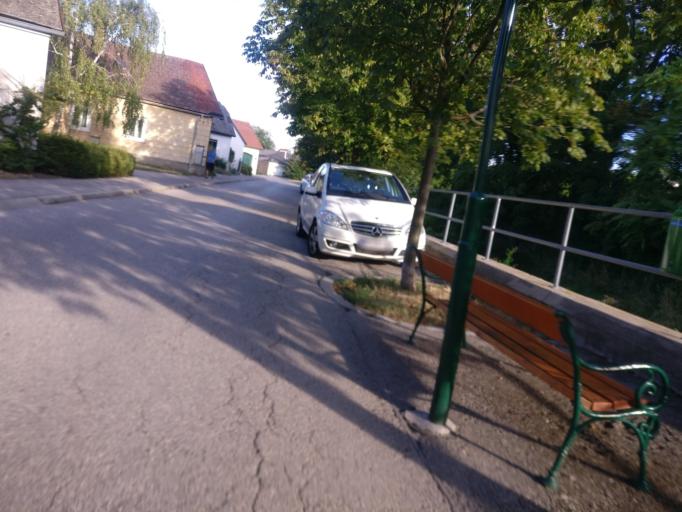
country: AT
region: Lower Austria
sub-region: Politischer Bezirk Modling
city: Wiener Neudorf
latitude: 48.0837
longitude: 16.3151
